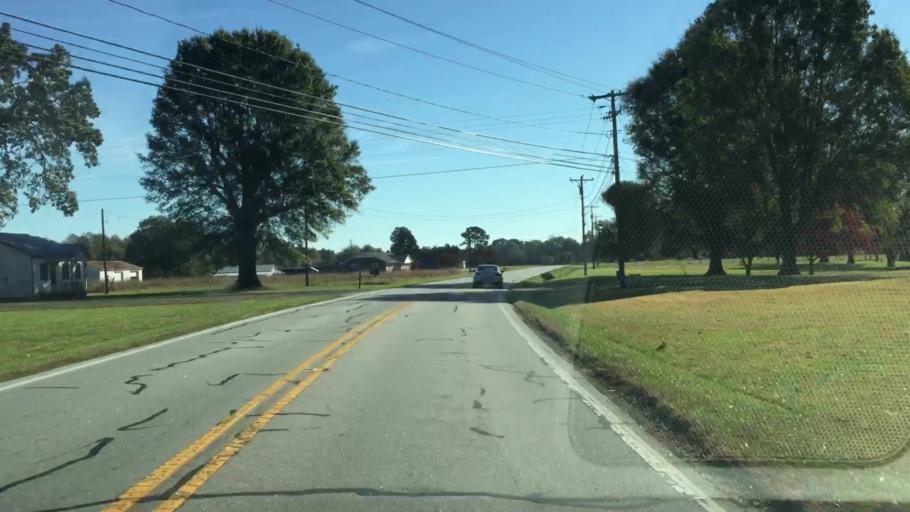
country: US
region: North Carolina
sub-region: Rowan County
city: China Grove
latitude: 35.6534
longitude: -80.5820
